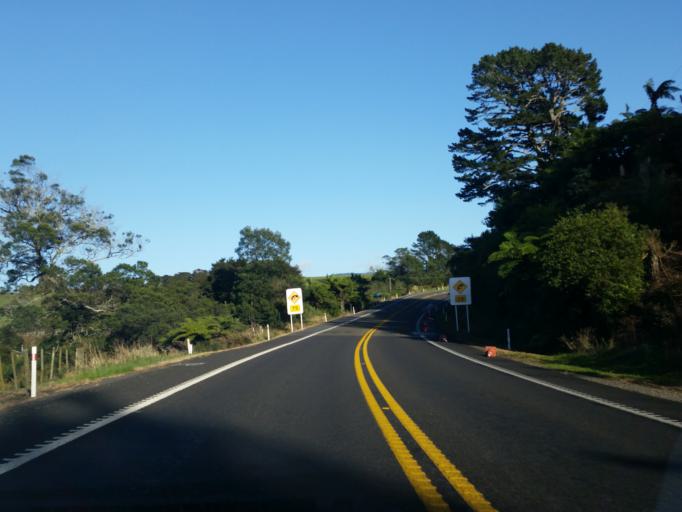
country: NZ
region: Bay of Plenty
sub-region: Western Bay of Plenty District
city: Katikati
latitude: -37.6498
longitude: 175.9722
